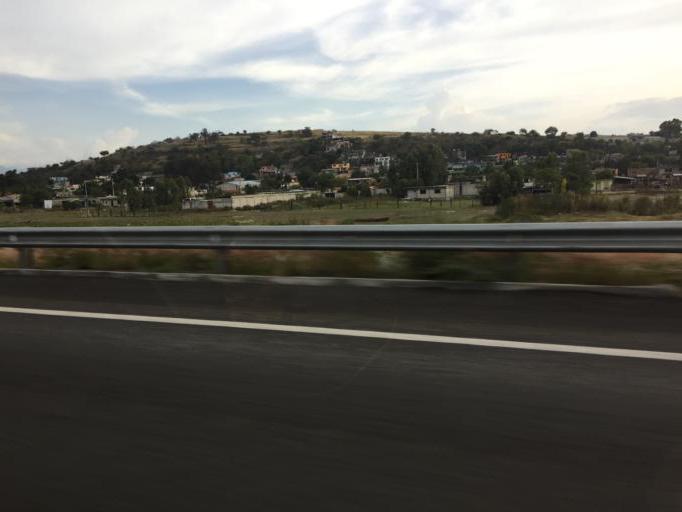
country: MX
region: Michoacan
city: Querendaro
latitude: 19.8852
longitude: -100.9470
